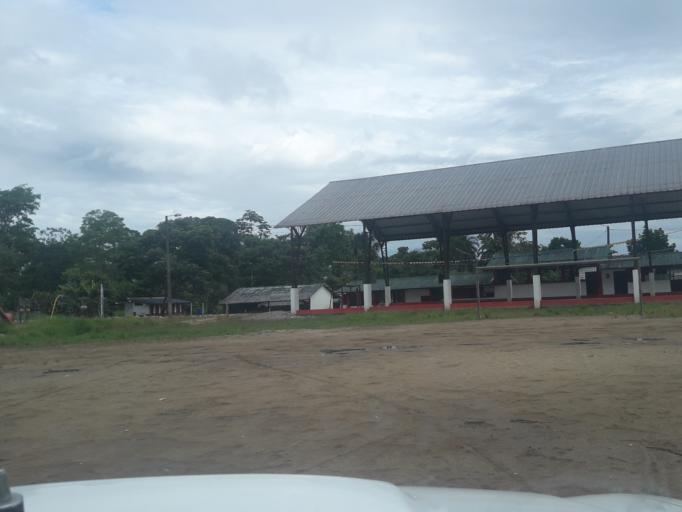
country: EC
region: Napo
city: Tena
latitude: -0.9556
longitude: -77.8155
